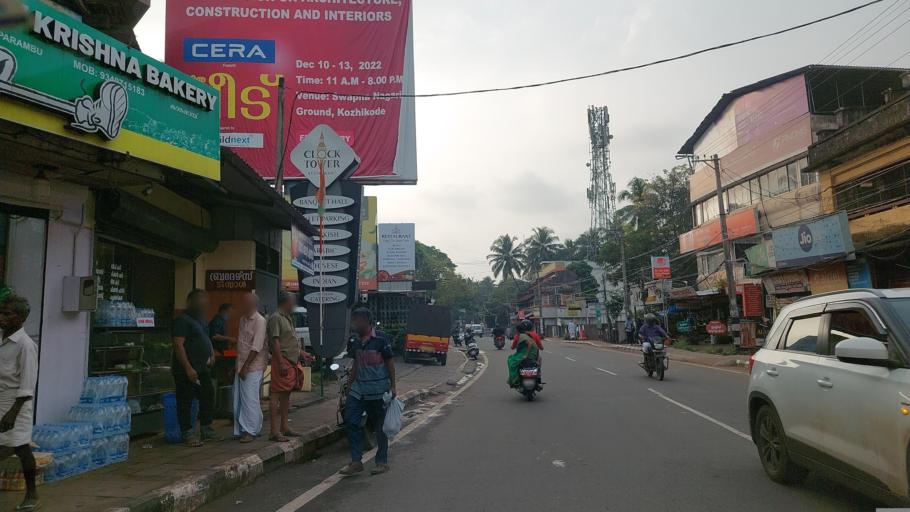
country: IN
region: Kerala
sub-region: Kozhikode
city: Kozhikode
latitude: 11.2870
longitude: 75.7816
